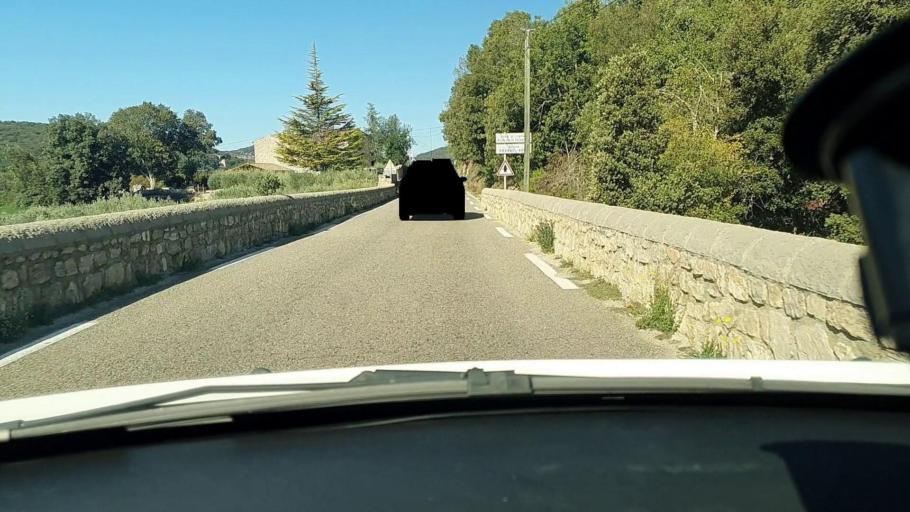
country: FR
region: Languedoc-Roussillon
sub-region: Departement du Gard
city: Goudargues
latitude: 44.2689
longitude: 4.4284
